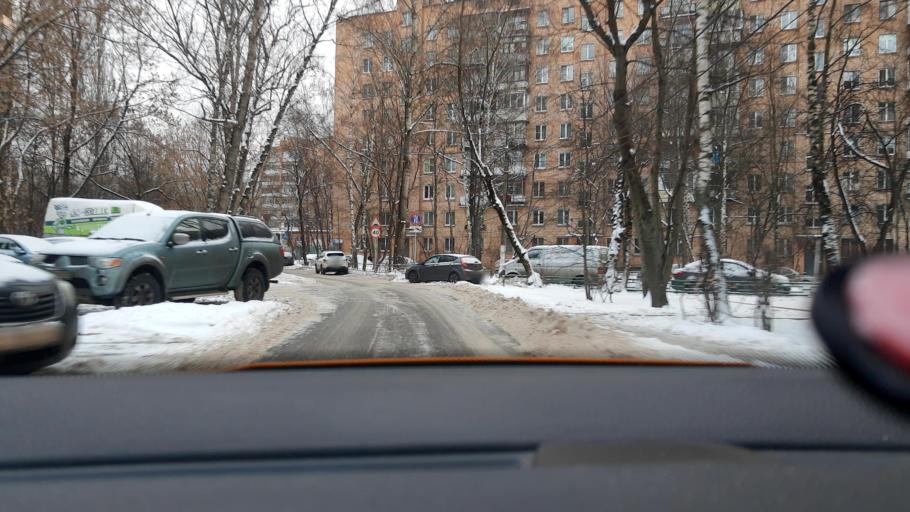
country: RU
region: Moskovskaya
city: Levoberezhnaya
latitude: 55.8891
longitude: 37.4773
